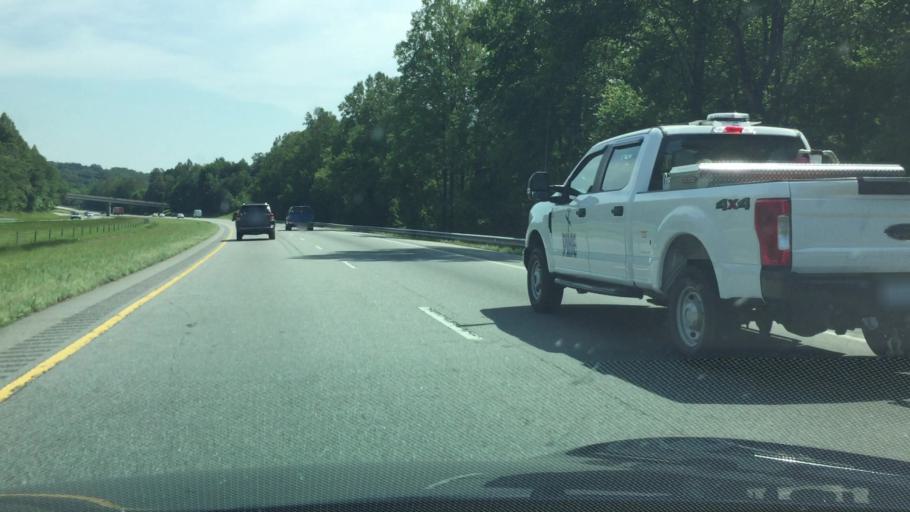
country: US
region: North Carolina
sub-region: Yadkin County
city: Yadkinville
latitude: 36.0243
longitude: -80.8224
